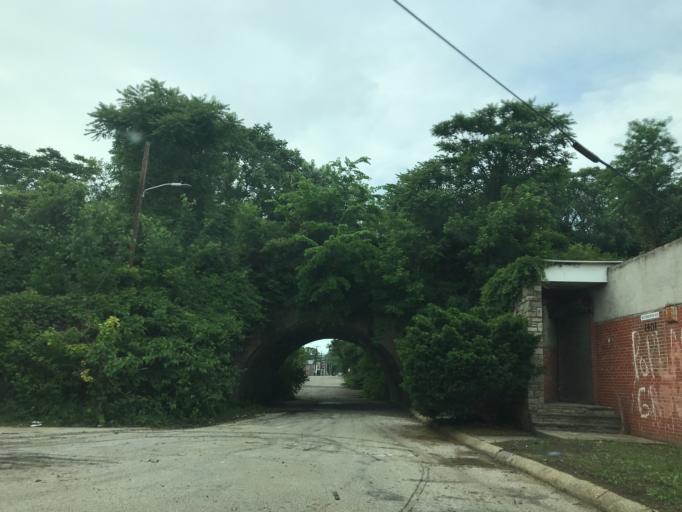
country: US
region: Maryland
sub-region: City of Baltimore
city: Baltimore
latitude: 39.3039
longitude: -76.6607
